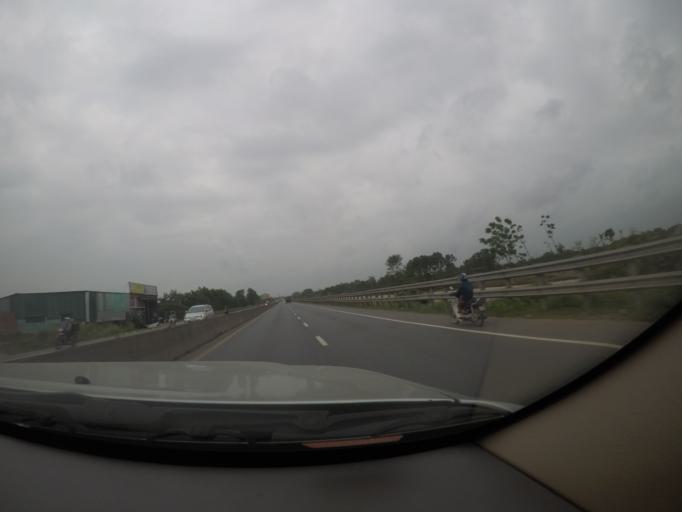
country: VN
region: Quang Tri
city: Hai Lang
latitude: 16.6373
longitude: 107.2983
